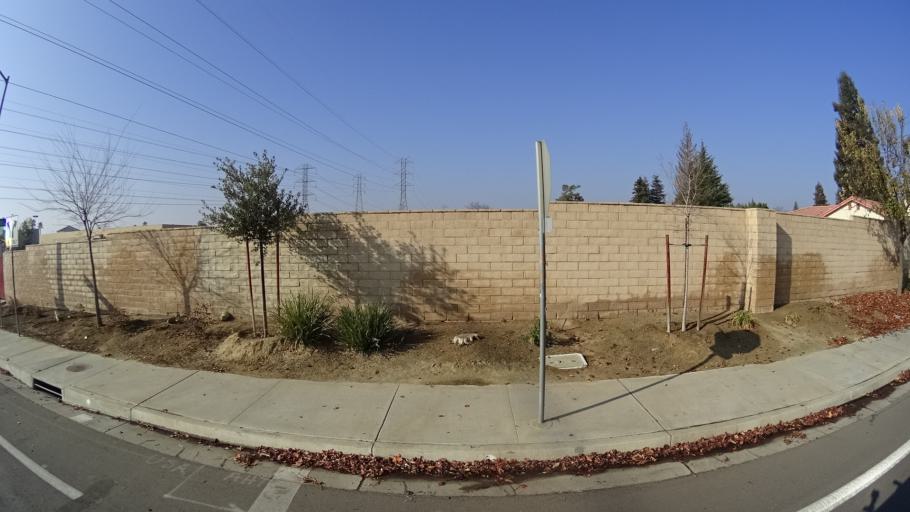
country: US
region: California
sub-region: Kern County
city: Greenacres
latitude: 35.3870
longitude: -119.1011
